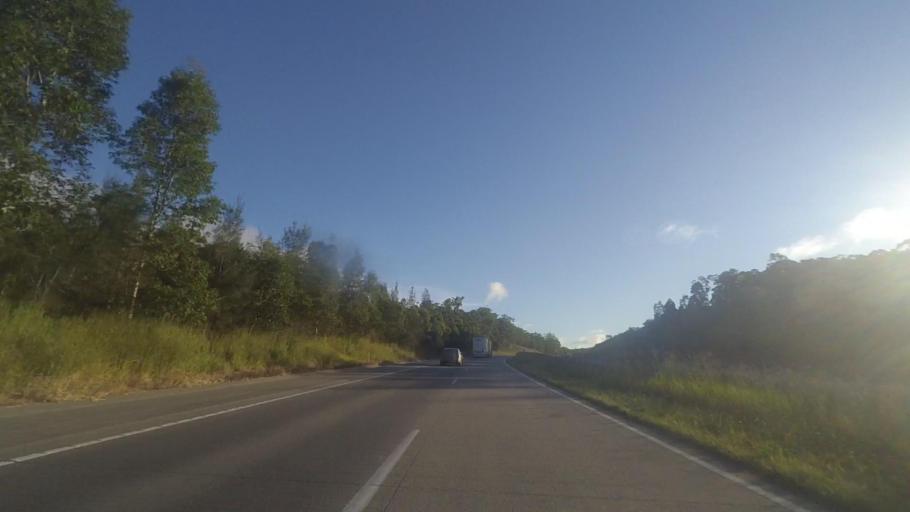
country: AU
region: New South Wales
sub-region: Great Lakes
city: Bulahdelah
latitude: -32.5136
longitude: 152.2101
